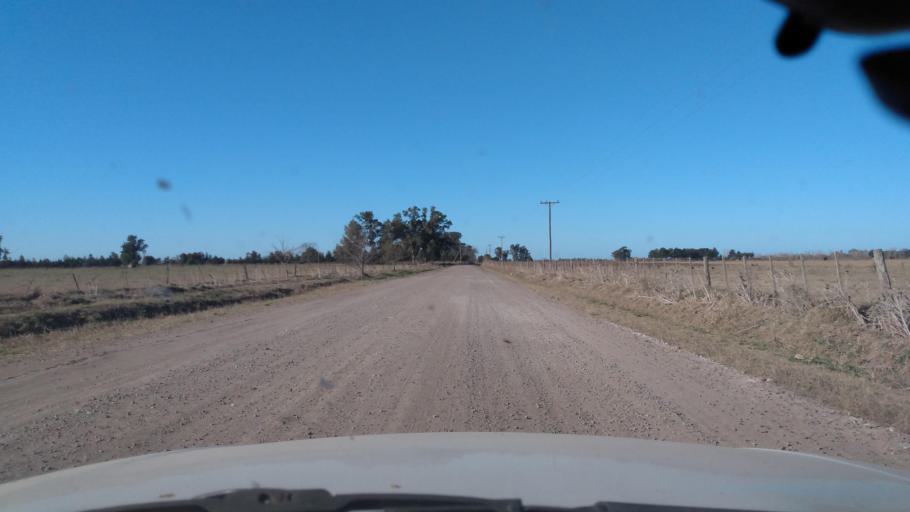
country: AR
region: Buenos Aires
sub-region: Partido de Mercedes
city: Mercedes
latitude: -34.6097
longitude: -59.3149
